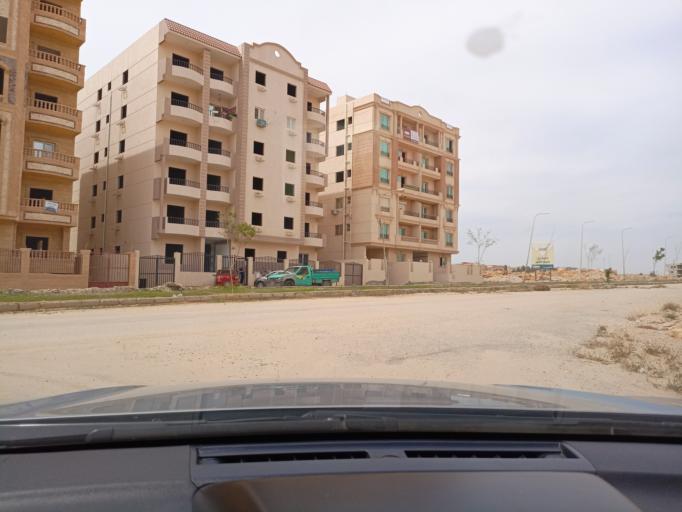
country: EG
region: Muhafazat al Qalyubiyah
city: Al Khankah
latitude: 30.2490
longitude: 31.5032
